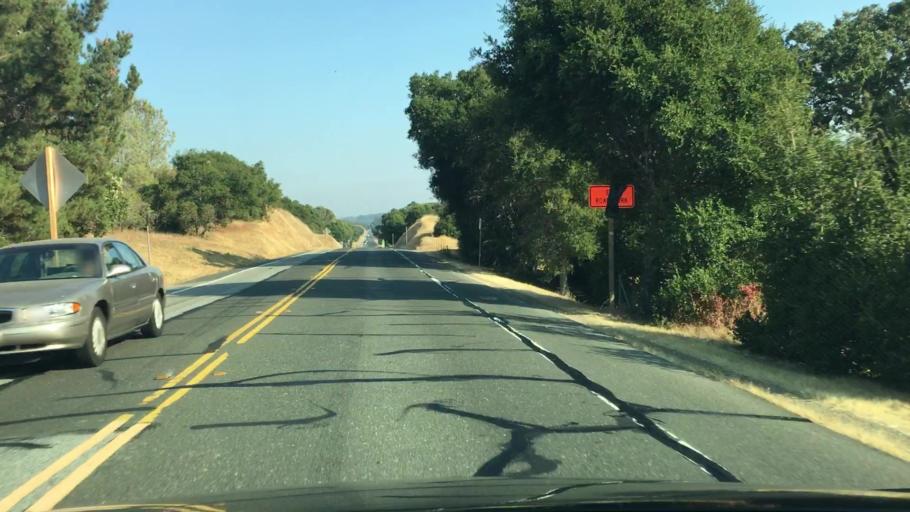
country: US
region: California
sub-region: San Mateo County
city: Emerald Lake Hills
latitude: 37.4815
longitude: -122.3136
